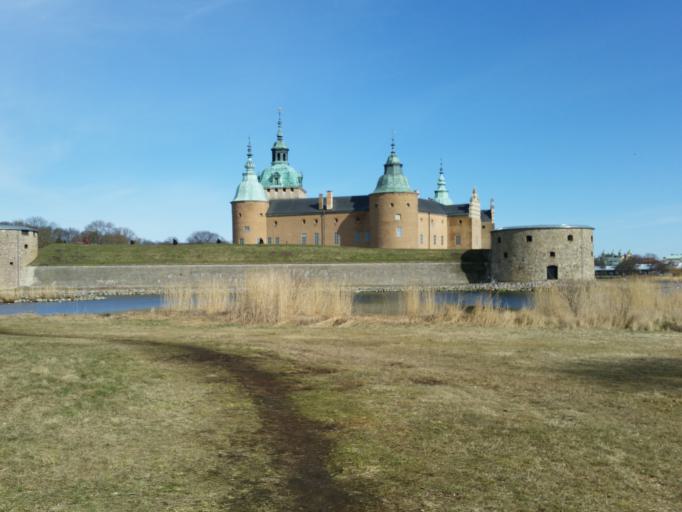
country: SE
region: Kalmar
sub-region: Kalmar Kommun
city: Kalmar
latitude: 56.6560
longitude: 16.3544
